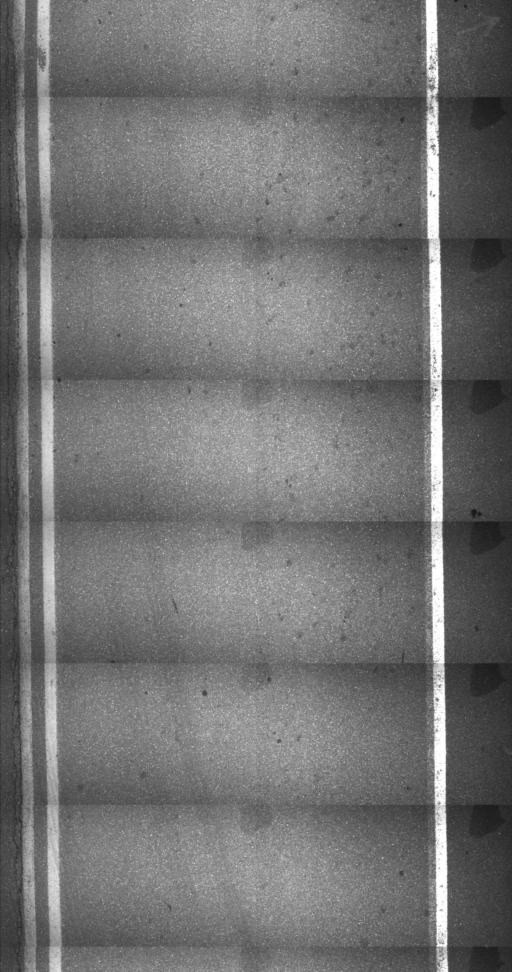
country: CA
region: Quebec
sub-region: Estrie
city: Coaticook
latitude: 44.9988
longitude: -71.7485
